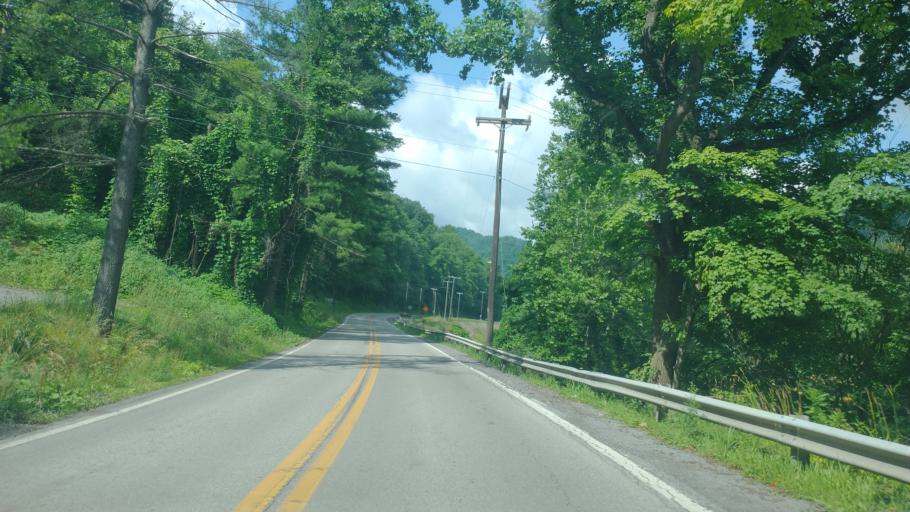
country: US
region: West Virginia
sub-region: McDowell County
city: Welch
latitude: 37.4118
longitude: -81.4535
